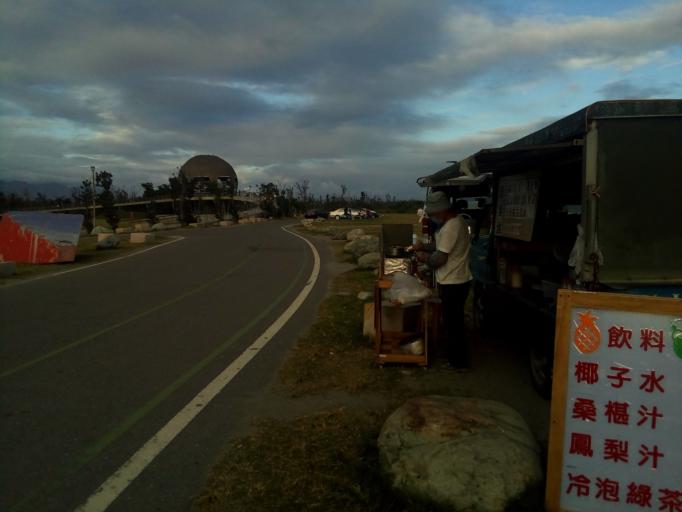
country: TW
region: Taiwan
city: Taitung City
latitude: 22.7519
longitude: 121.1640
